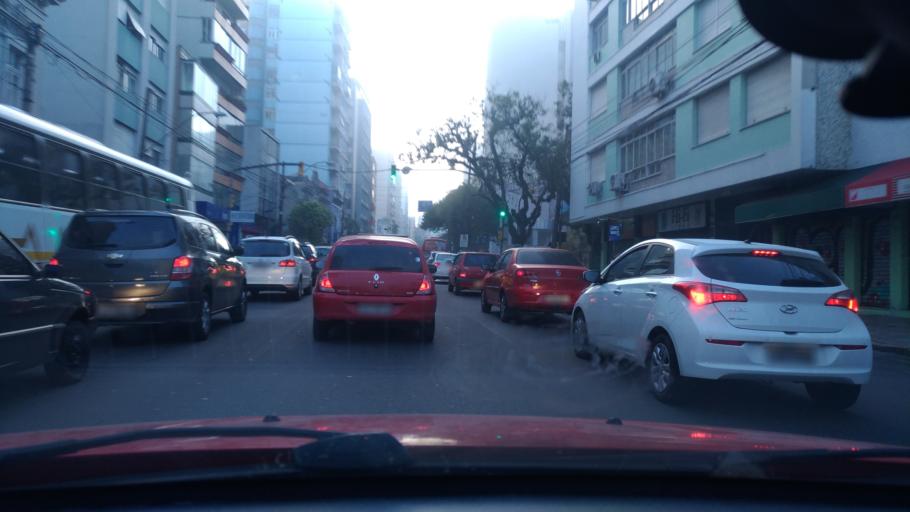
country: BR
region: Rio Grande do Sul
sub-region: Porto Alegre
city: Porto Alegre
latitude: -30.0293
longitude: -51.2164
